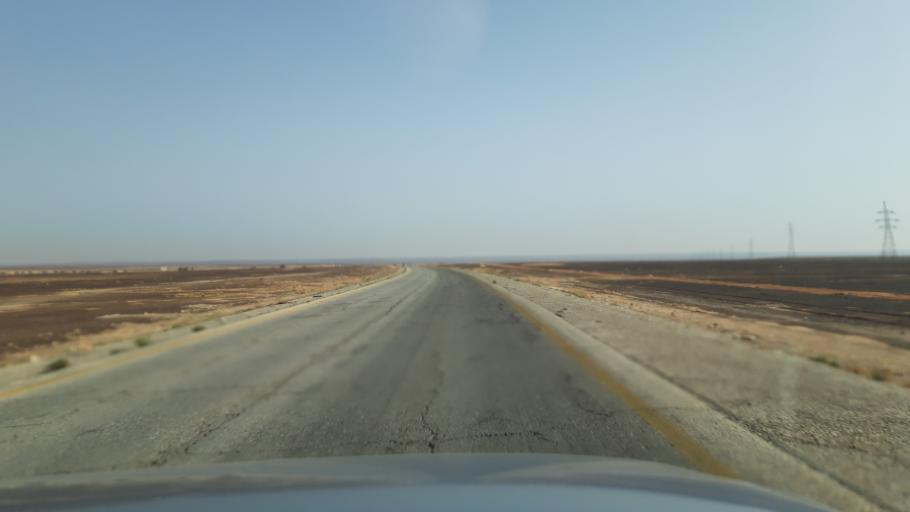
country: JO
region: Amman
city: Al Azraq ash Shamali
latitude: 31.7871
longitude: 36.5799
